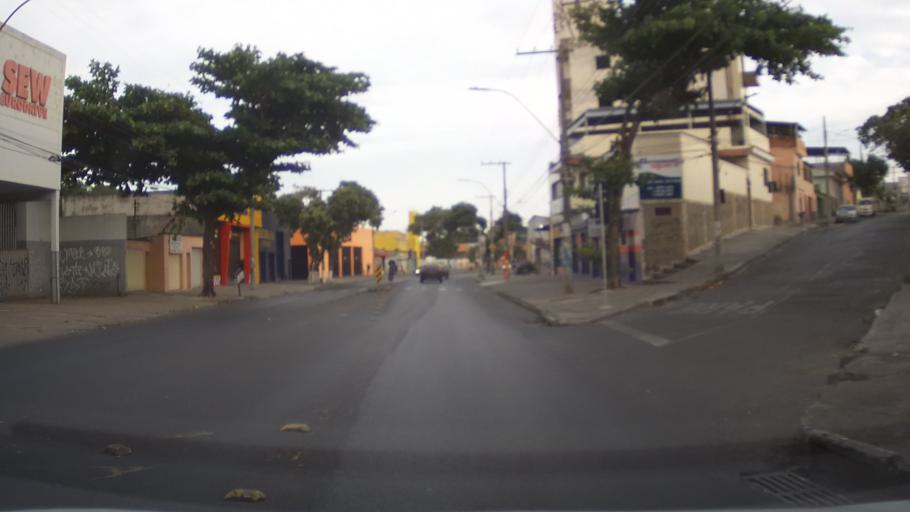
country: BR
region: Minas Gerais
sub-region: Contagem
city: Contagem
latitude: -19.9049
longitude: -44.0059
